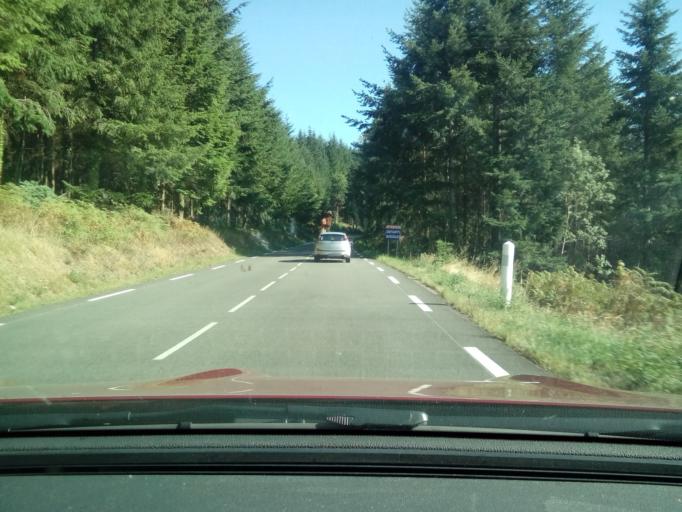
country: FR
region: Rhone-Alpes
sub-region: Departement du Rhone
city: Cublize
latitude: 45.9744
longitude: 4.3911
